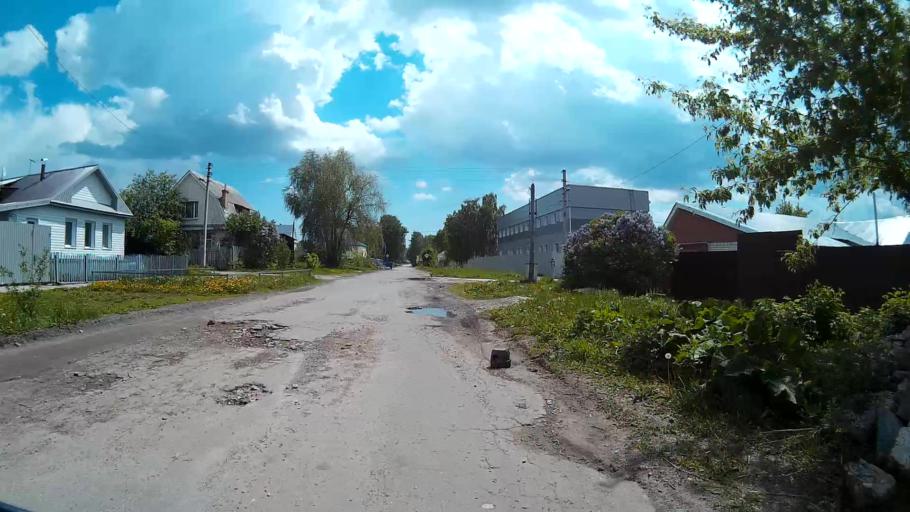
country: RU
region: Ulyanovsk
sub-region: Ulyanovskiy Rayon
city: Ulyanovsk
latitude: 54.3452
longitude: 48.3608
